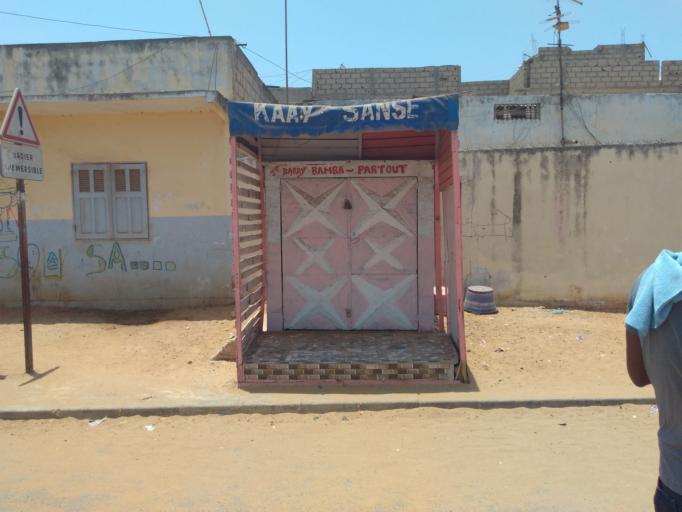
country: SN
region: Dakar
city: Pikine
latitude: 14.7799
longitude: -17.3751
